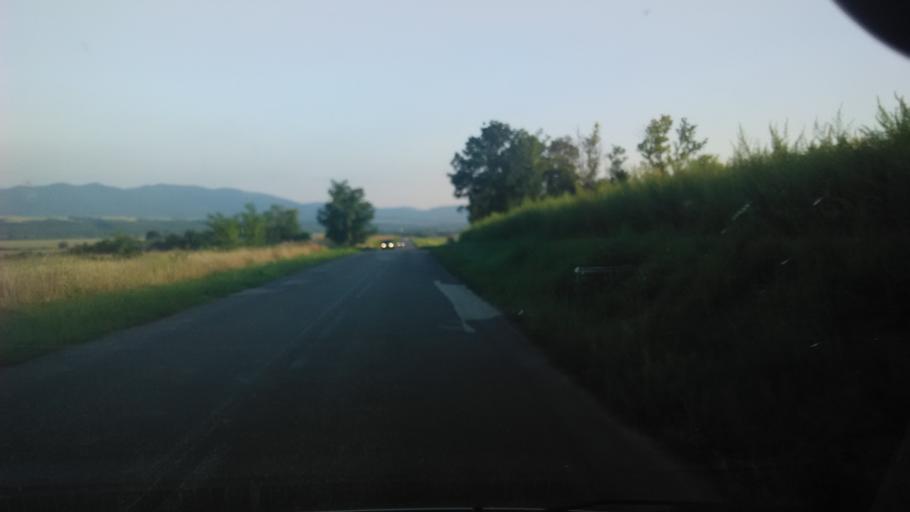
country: SK
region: Nitriansky
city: Zeliezovce
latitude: 48.0492
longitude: 18.7980
